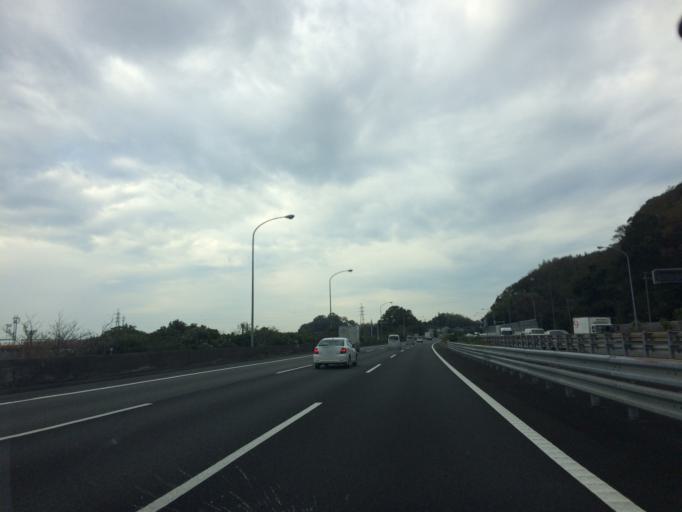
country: JP
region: Shizuoka
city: Yaizu
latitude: 34.8945
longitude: 138.3311
